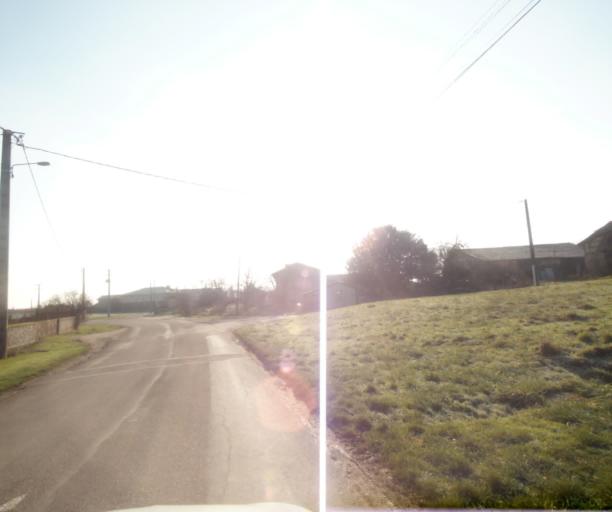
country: FR
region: Champagne-Ardenne
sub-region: Departement de la Haute-Marne
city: Montier-en-Der
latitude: 48.4786
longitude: 4.7531
